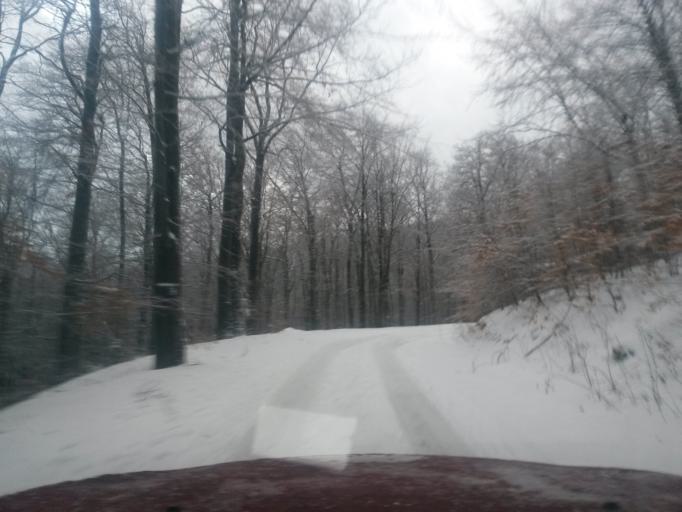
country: SK
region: Kosicky
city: Kosice
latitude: 48.7627
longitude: 21.1270
